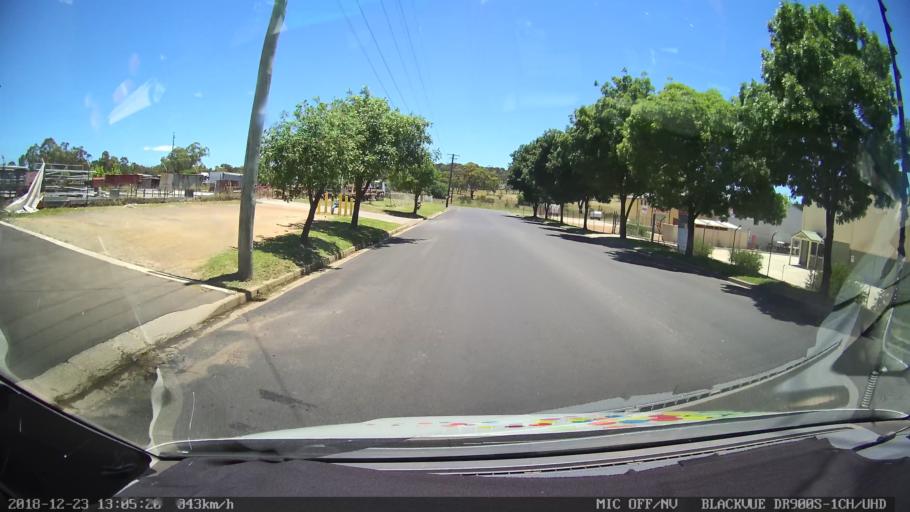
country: AU
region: New South Wales
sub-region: Armidale Dumaresq
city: Armidale
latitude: -30.5148
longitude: 151.6425
